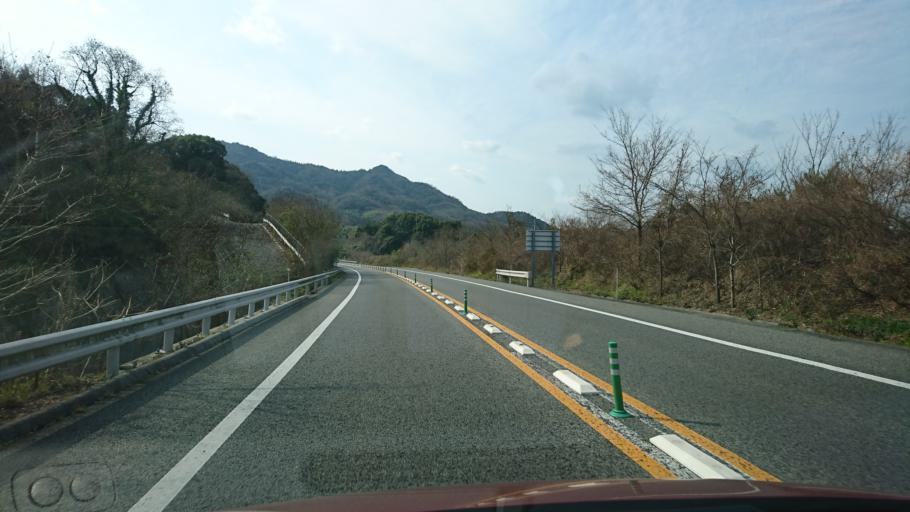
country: JP
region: Hiroshima
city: Innoshima
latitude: 34.1316
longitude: 133.0445
